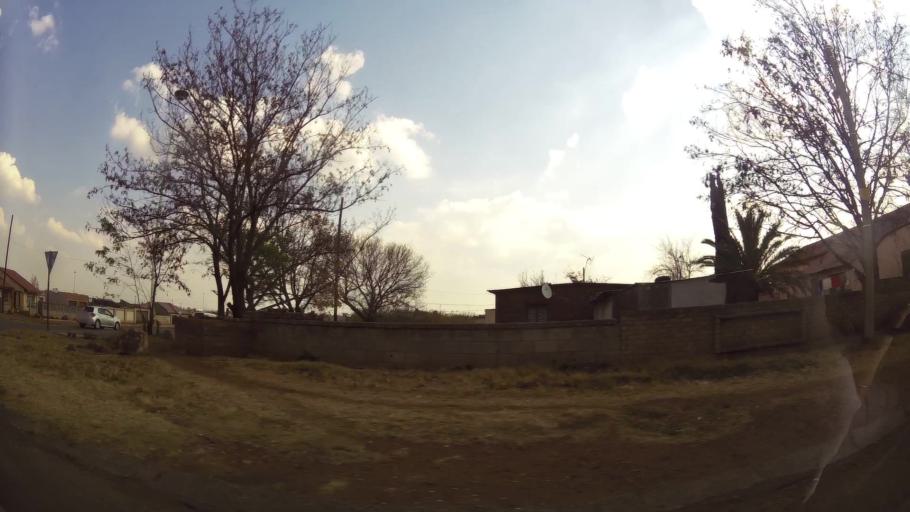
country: ZA
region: Gauteng
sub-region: Ekurhuleni Metropolitan Municipality
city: Germiston
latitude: -26.3440
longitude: 28.1547
